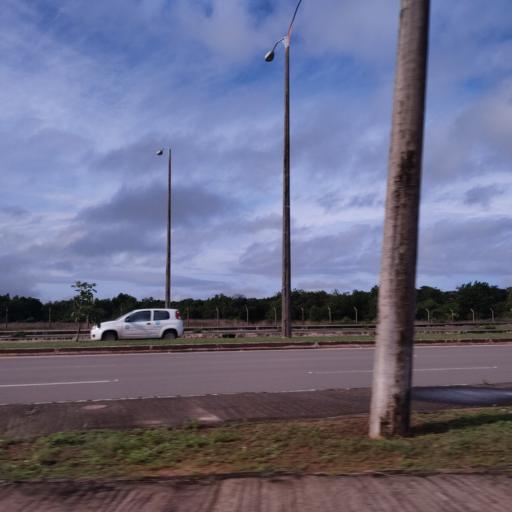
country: BR
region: Maranhao
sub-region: Sao Luis
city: Sao Luis
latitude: -2.5119
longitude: -44.2736
